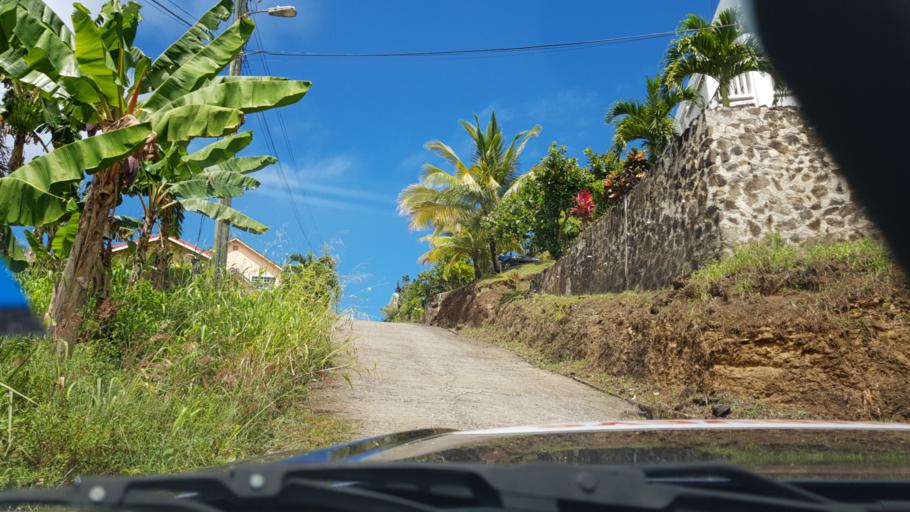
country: LC
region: Anse-la-Raye
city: Anse La Raye
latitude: 13.9438
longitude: -61.0358
